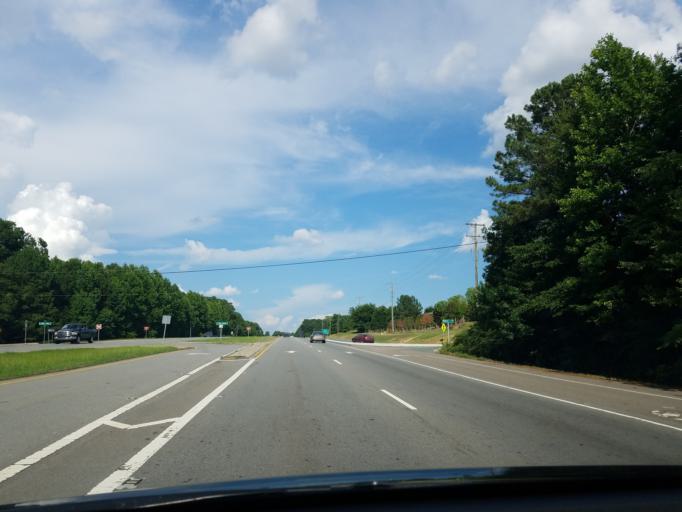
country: US
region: North Carolina
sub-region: Wake County
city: Apex
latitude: 35.7490
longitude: -78.8657
